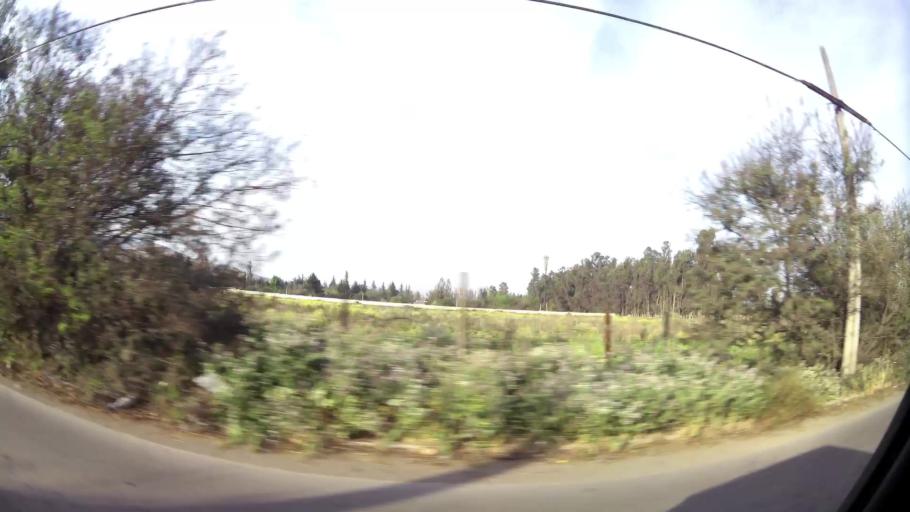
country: CL
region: Santiago Metropolitan
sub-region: Provincia de Maipo
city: San Bernardo
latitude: -33.5610
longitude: -70.7632
